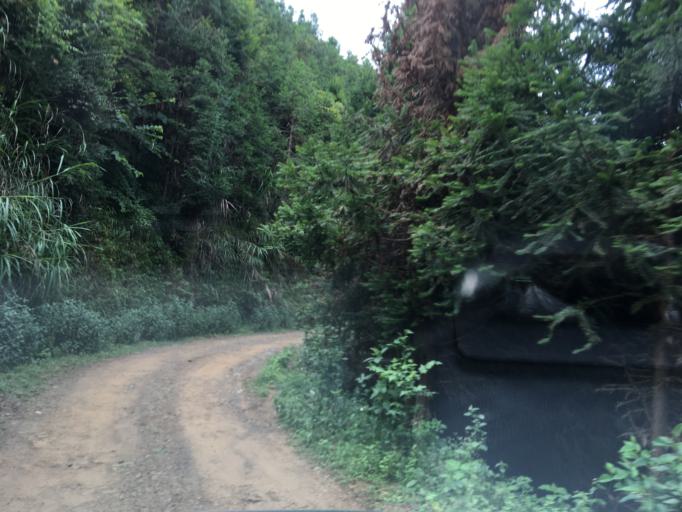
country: CN
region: Guangxi Zhuangzu Zizhiqu
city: Xinzhou
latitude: 24.8779
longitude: 105.8458
